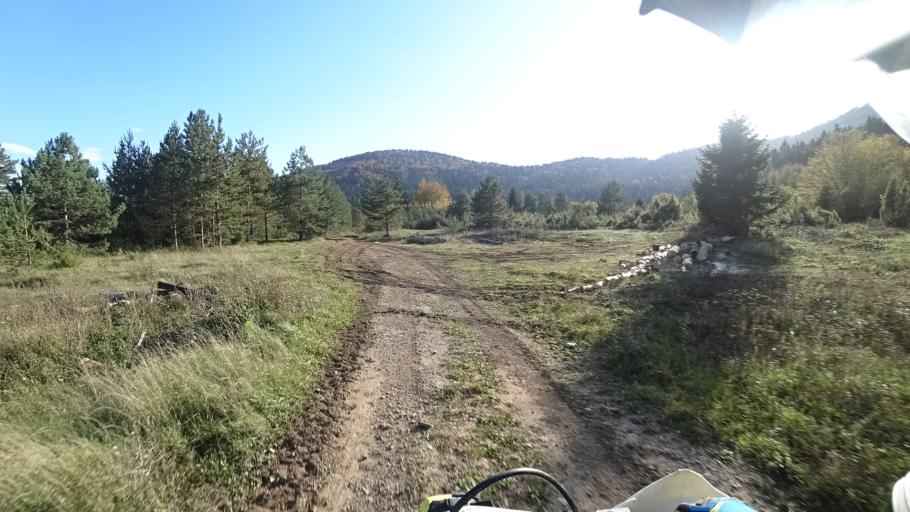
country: HR
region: Karlovacka
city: Plaski
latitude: 45.0010
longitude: 15.4072
